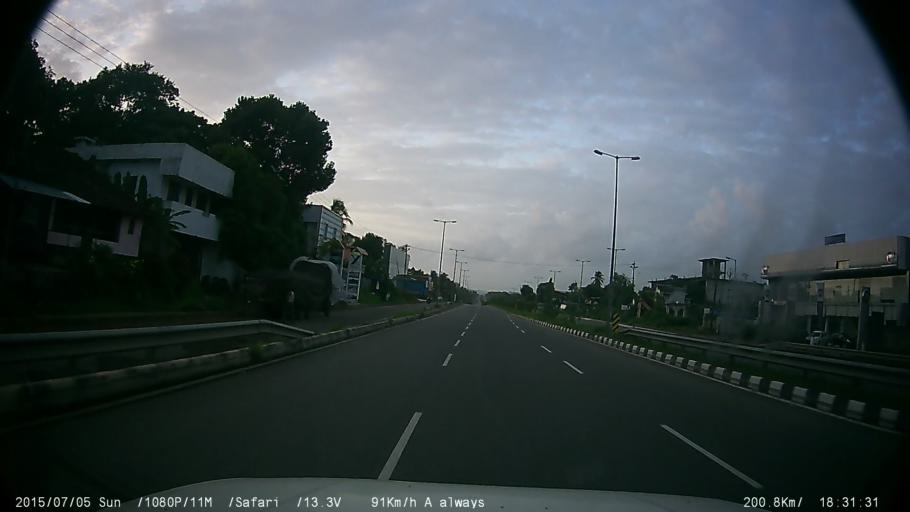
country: IN
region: Kerala
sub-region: Thrissur District
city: Trichur
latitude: 10.4958
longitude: 76.2580
